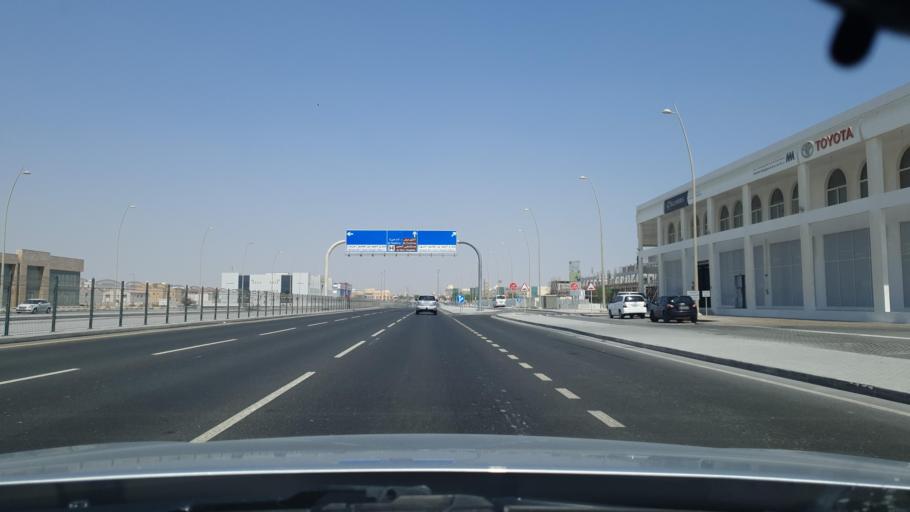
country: QA
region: Al Khawr
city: Al Khawr
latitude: 25.6679
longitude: 51.5011
